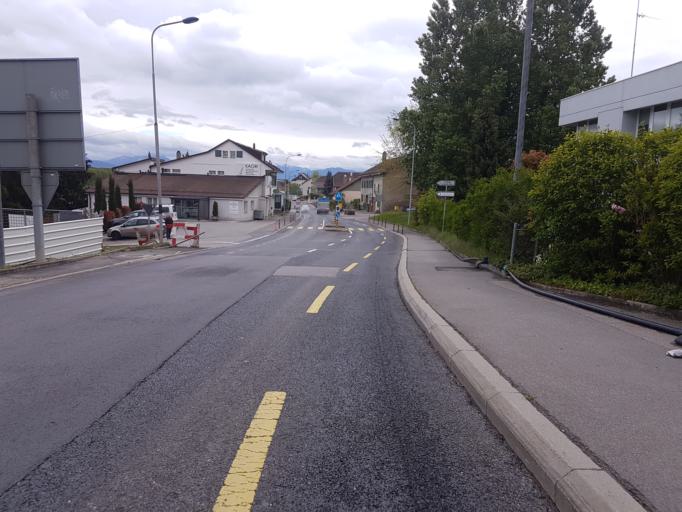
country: CH
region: Vaud
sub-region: Morges District
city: Preverenges
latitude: 46.5275
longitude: 6.5417
